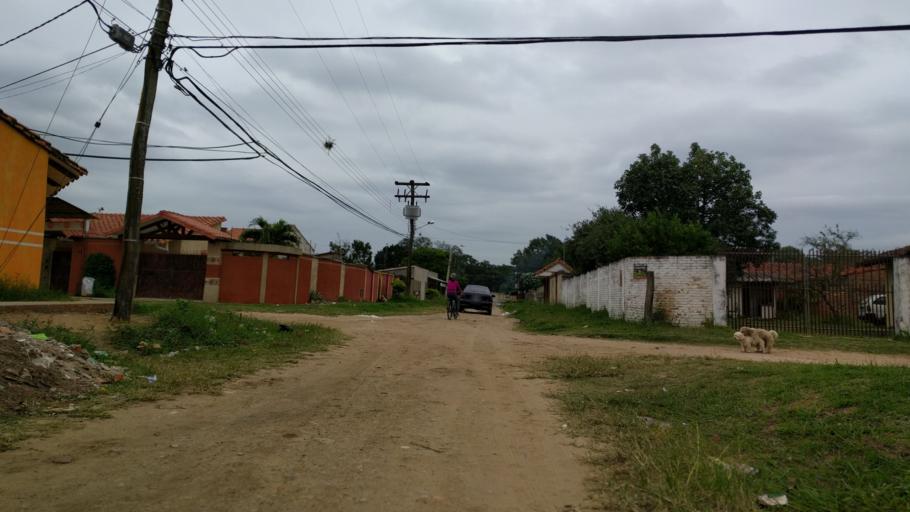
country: BO
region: Santa Cruz
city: Santa Cruz de la Sierra
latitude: -17.8065
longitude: -63.2175
